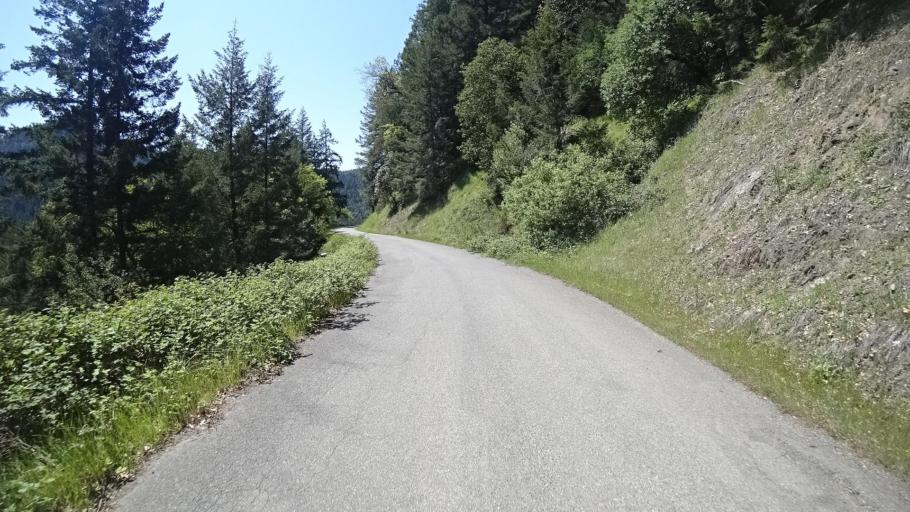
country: US
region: California
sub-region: Humboldt County
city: Redway
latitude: 40.1922
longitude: -123.5288
